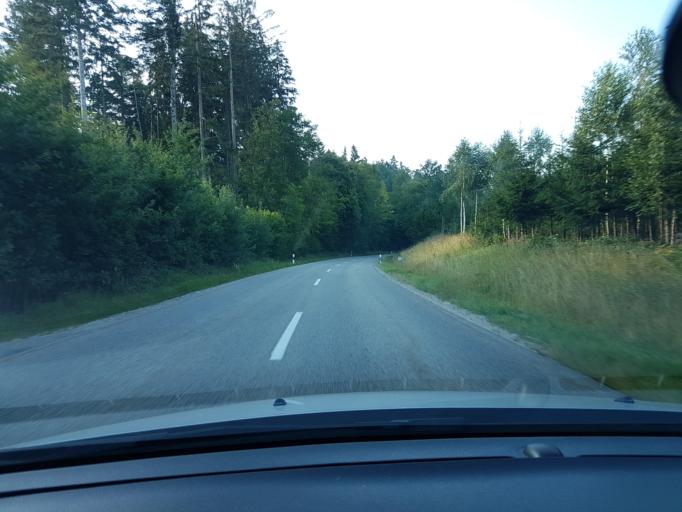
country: DE
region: Bavaria
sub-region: Upper Bavaria
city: Egglkofen
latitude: 48.4575
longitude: 12.4738
